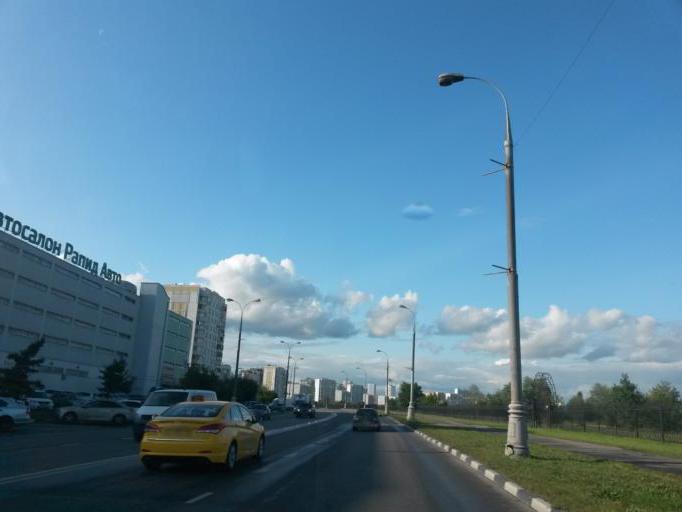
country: RU
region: Moscow
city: Brateyevo
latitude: 55.6538
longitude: 37.7779
